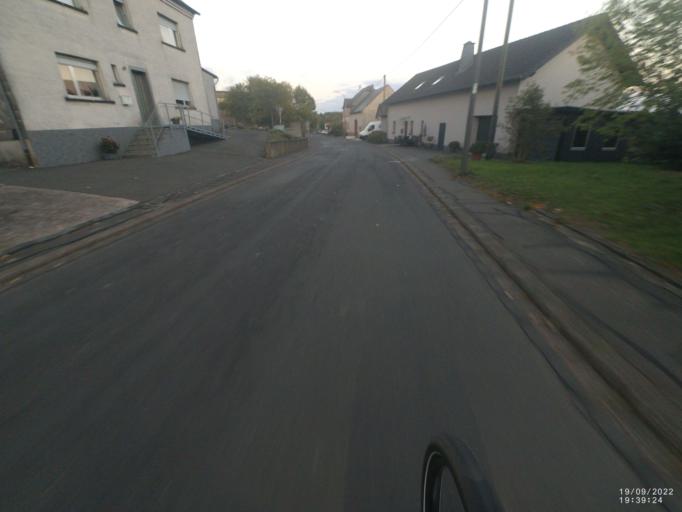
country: DE
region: Rheinland-Pfalz
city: Brockscheid
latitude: 50.1324
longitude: 6.8458
